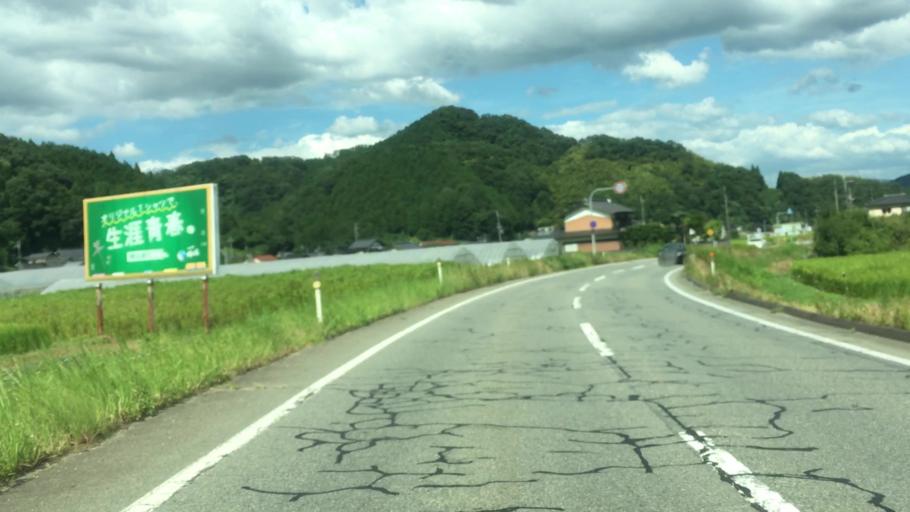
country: JP
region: Hyogo
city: Toyooka
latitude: 35.4650
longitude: 134.7447
